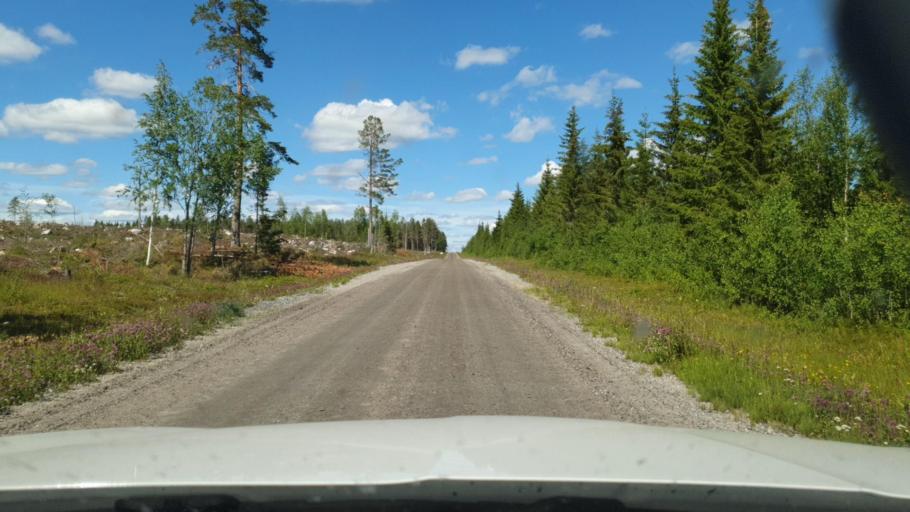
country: SE
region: Vaesterbotten
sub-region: Skelleftea Kommun
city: Byske
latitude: 65.1299
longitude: 21.1993
